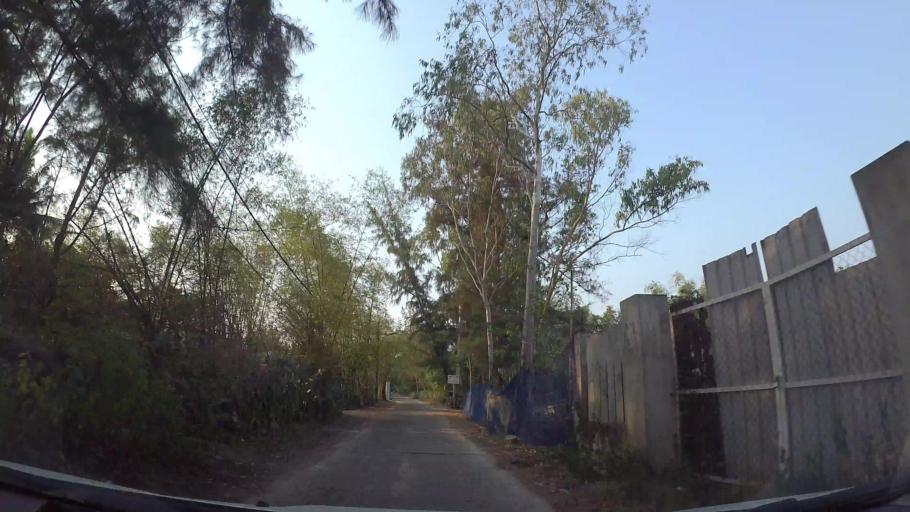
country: VN
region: Da Nang
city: Ngu Hanh Son
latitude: 15.9710
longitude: 108.2440
